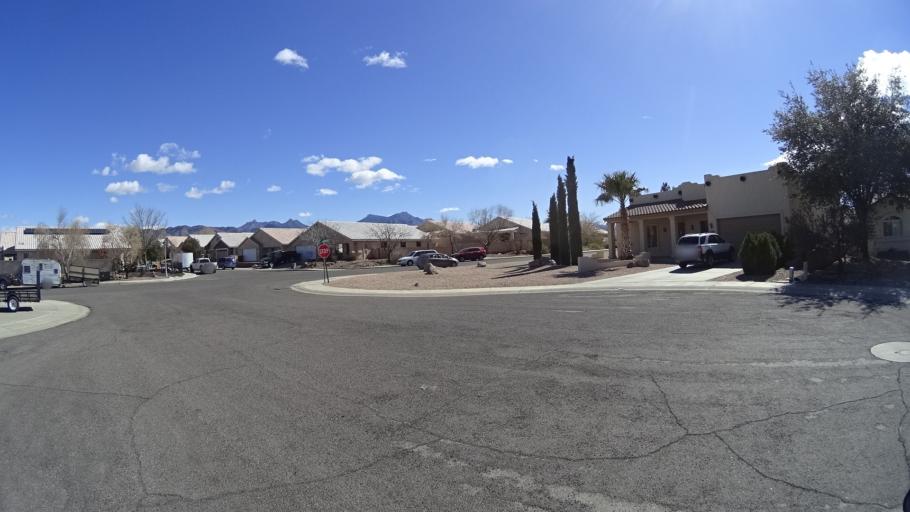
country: US
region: Arizona
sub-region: Mohave County
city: Kingman
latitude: 35.1898
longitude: -114.0094
